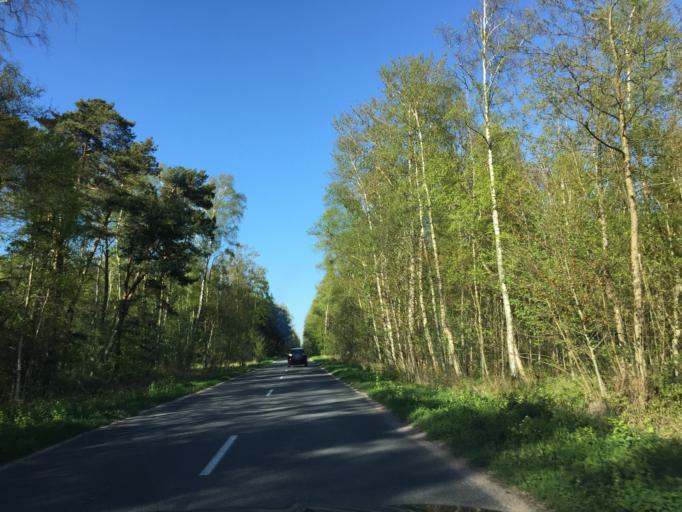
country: LT
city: Nida
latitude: 55.2161
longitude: 20.8841
